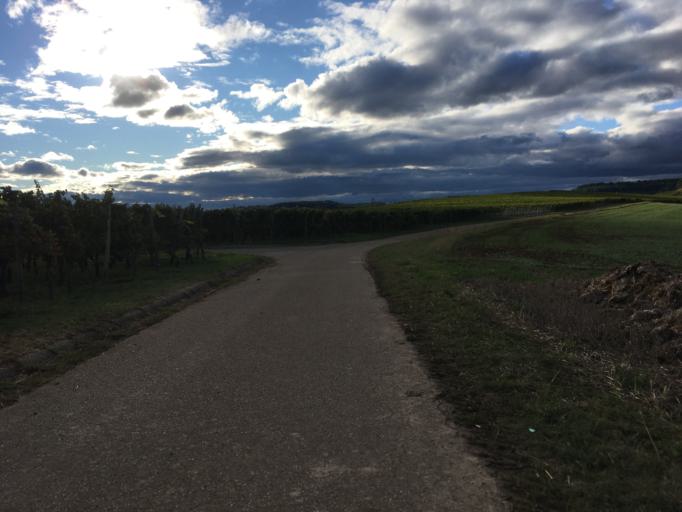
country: DE
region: Baden-Wuerttemberg
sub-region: Regierungsbezirk Stuttgart
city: Brackenheim
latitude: 49.0939
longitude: 9.0578
